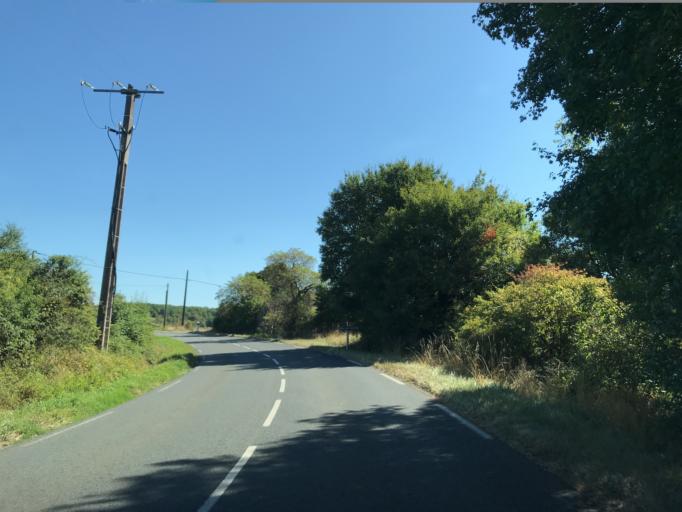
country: FR
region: Limousin
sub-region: Departement de la Correze
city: Larche
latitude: 45.0464
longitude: 1.3756
